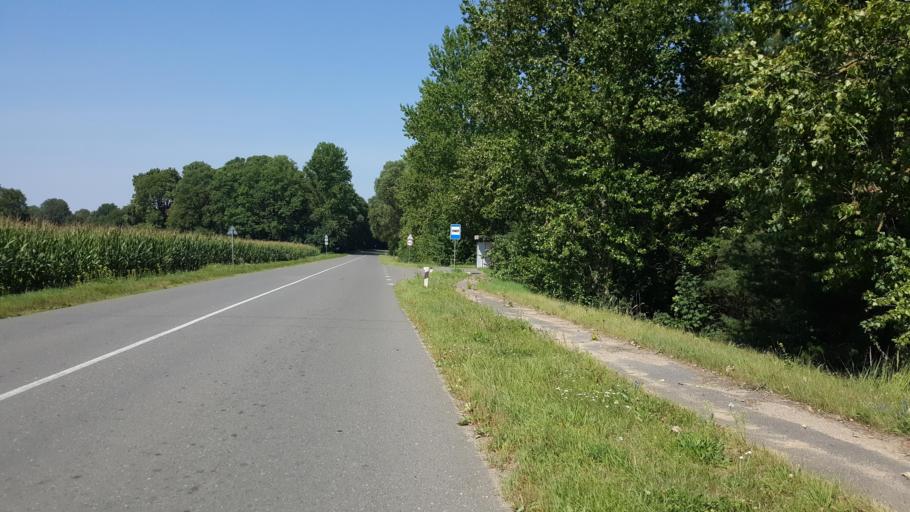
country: BY
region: Brest
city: Kamyanyuki
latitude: 52.4905
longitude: 23.6882
